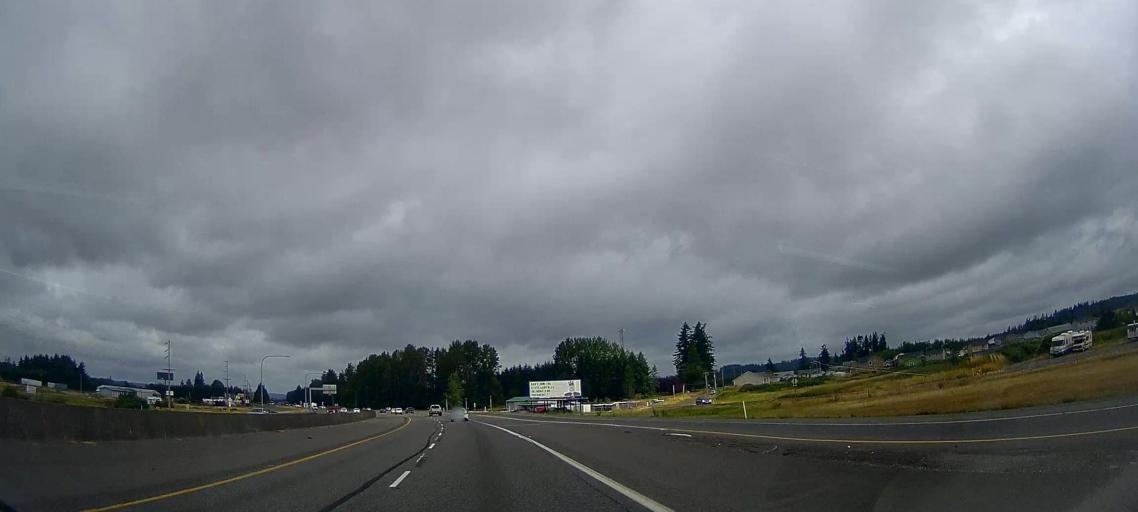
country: US
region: Washington
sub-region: Lewis County
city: Napavine
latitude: 46.6073
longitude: -122.9080
